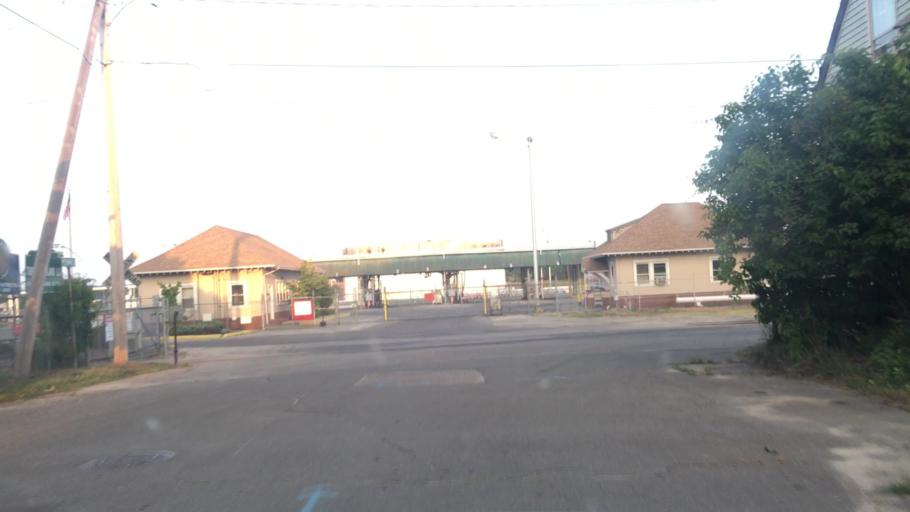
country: US
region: Maine
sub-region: Cumberland County
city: Portland
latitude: 43.6376
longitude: -70.2685
